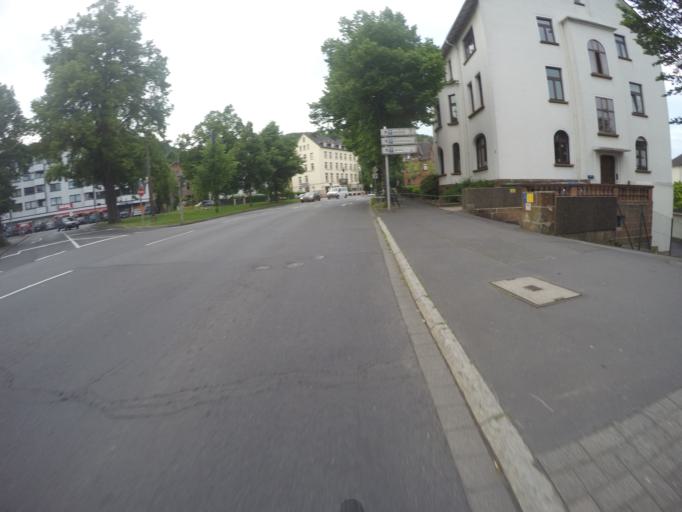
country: DE
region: Hesse
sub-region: Regierungsbezirk Giessen
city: Marburg an der Lahn
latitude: 50.8043
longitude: 8.7591
